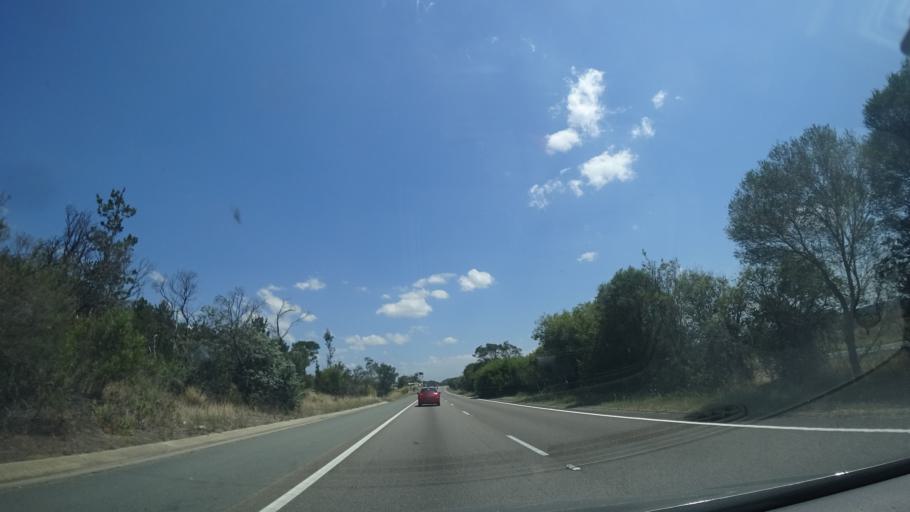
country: AU
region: New South Wales
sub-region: Wingecarribee
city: Bundanoon
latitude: -34.6024
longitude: 150.2342
